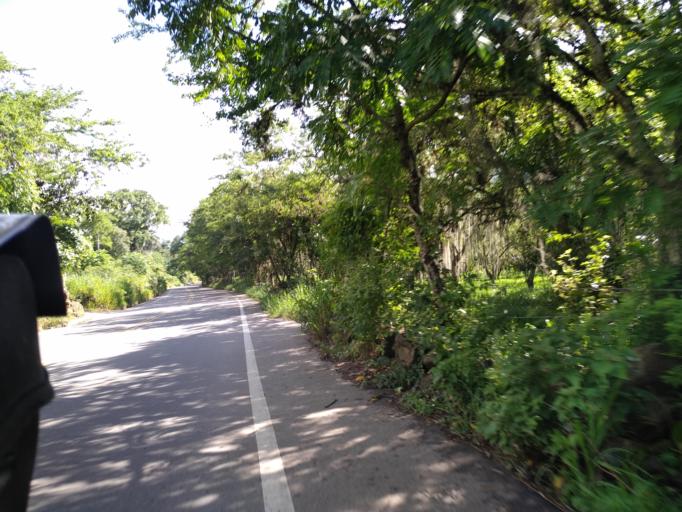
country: CO
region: Santander
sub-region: San Gil
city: San Gil
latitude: 6.5213
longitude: -73.1252
